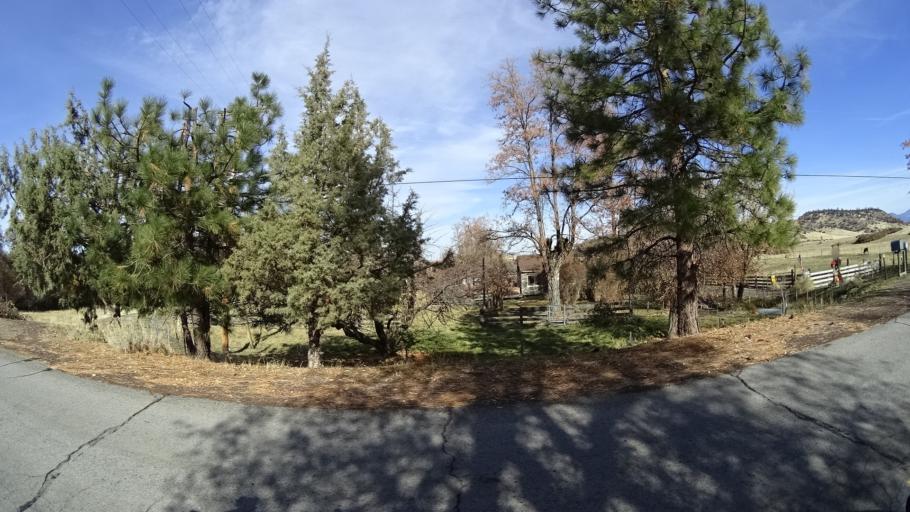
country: US
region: California
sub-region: Siskiyou County
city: Weed
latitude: 41.4711
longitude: -122.4395
